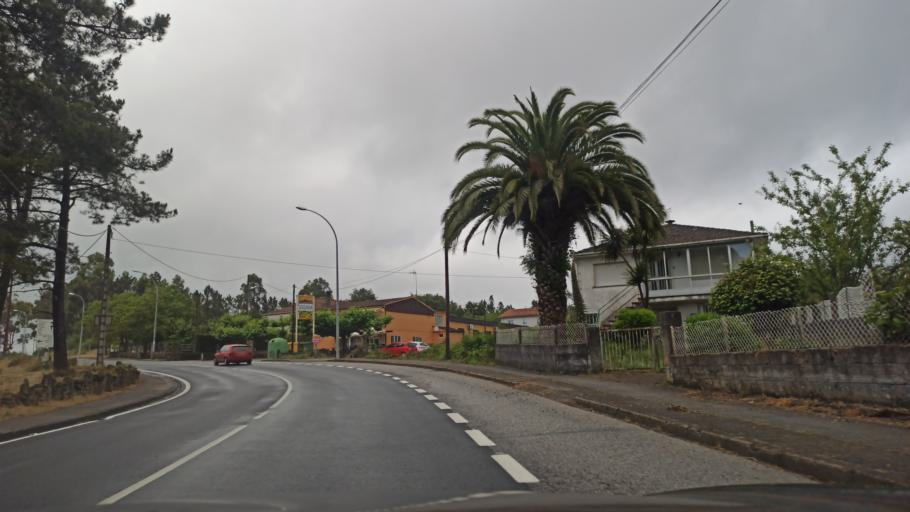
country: ES
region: Galicia
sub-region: Provincia da Coruna
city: Santiso
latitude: 42.7669
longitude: -8.0217
